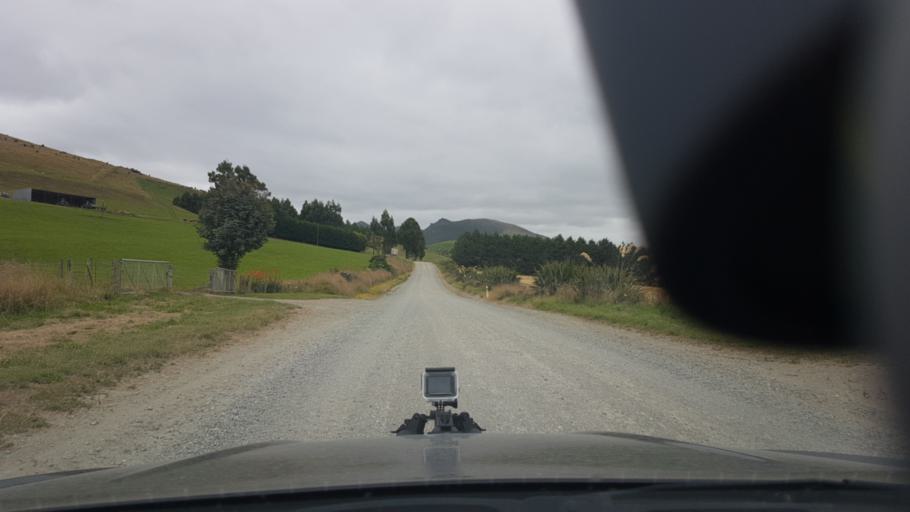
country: NZ
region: Otago
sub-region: Clutha District
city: Papatowai
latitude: -46.3443
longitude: 169.4354
